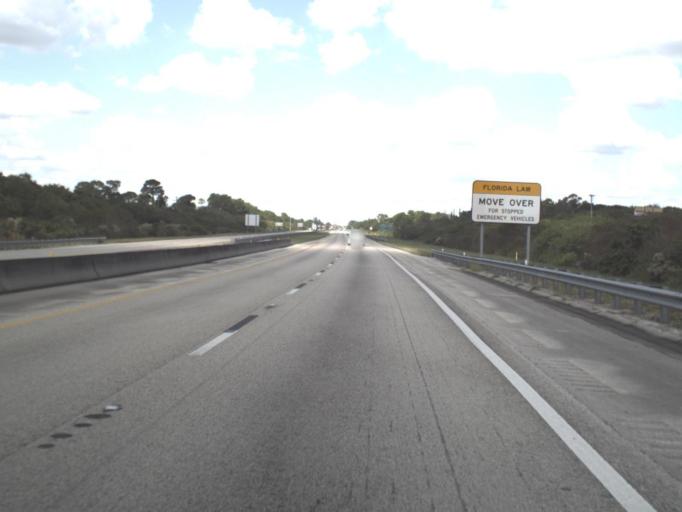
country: US
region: Florida
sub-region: Saint Lucie County
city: Fort Pierce South
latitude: 27.4161
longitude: -80.4041
